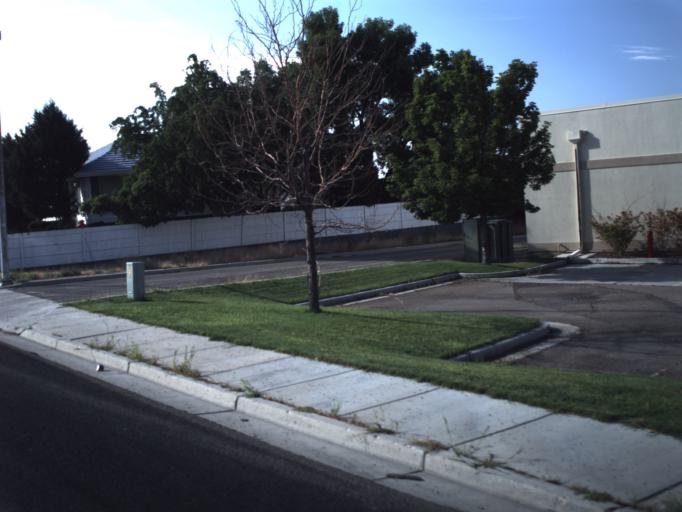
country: US
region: Utah
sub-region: Carbon County
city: Price
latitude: 39.5983
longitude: -110.7933
